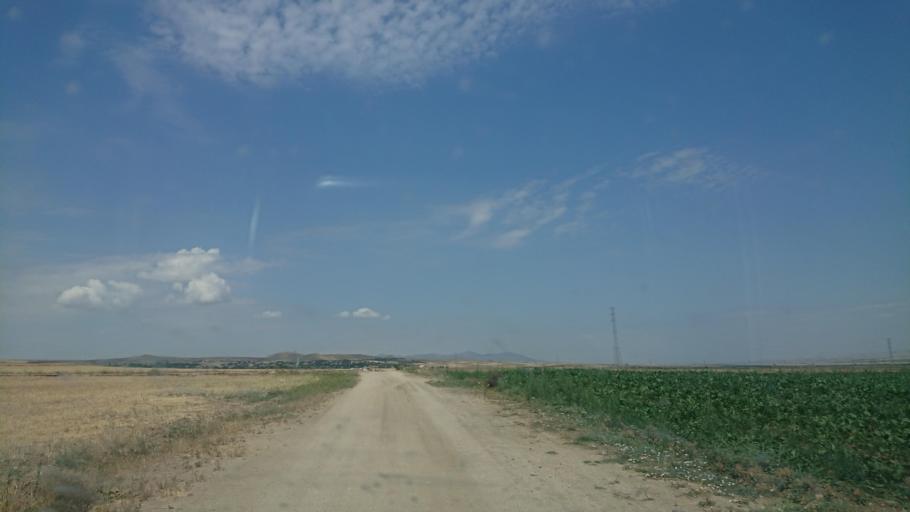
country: TR
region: Aksaray
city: Sariyahsi
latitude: 38.9567
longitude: 33.9148
